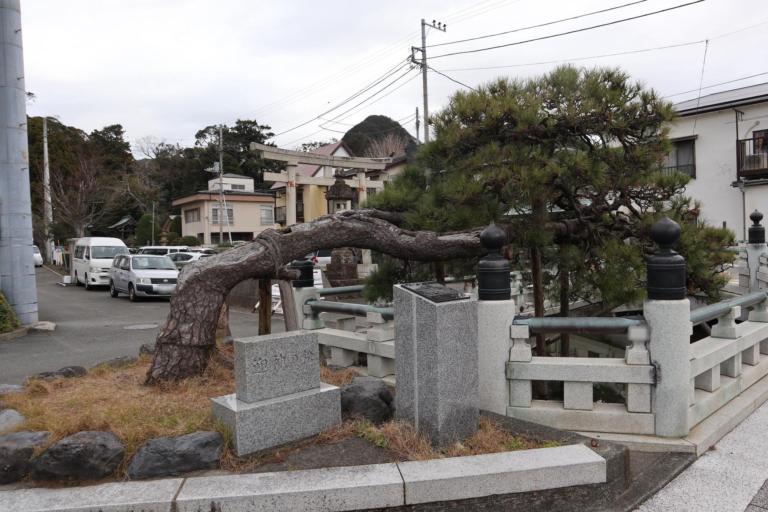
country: JP
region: Shizuoka
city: Shimoda
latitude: 34.6757
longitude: 138.9429
